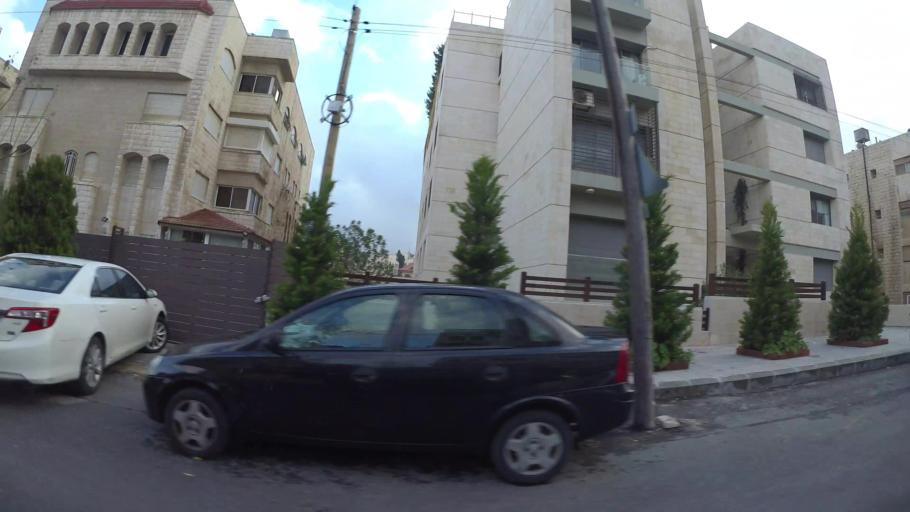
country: JO
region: Amman
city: Amman
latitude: 31.9549
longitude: 35.8882
